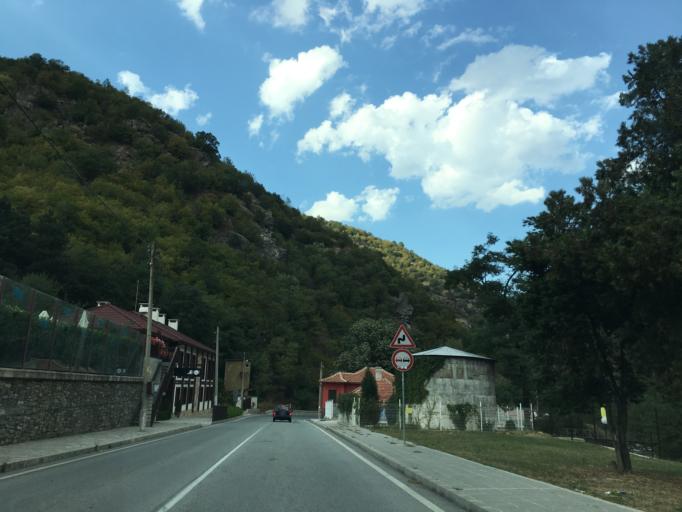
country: BG
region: Pazardzhik
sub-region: Obshtina Septemvri
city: Septemvri
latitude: 42.1338
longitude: 24.1246
